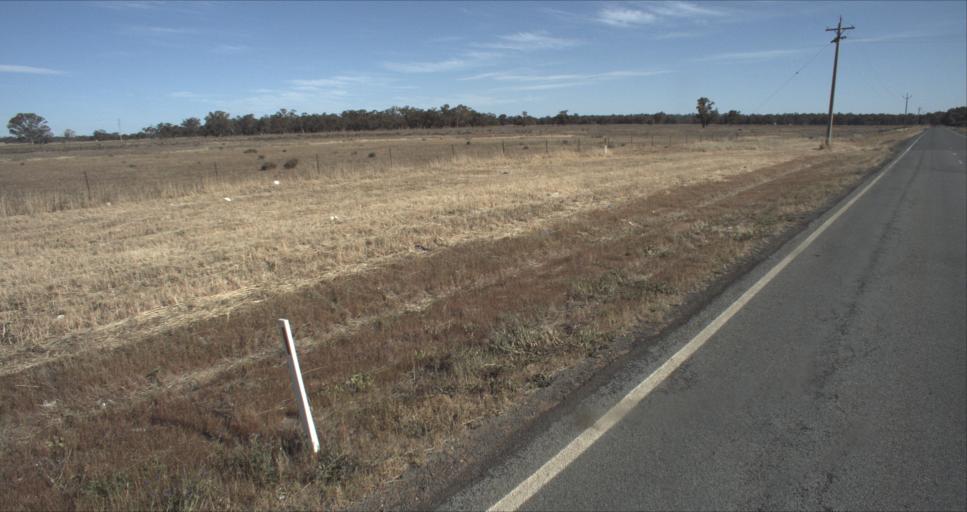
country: AU
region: New South Wales
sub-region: Leeton
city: Leeton
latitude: -34.6146
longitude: 146.4019
